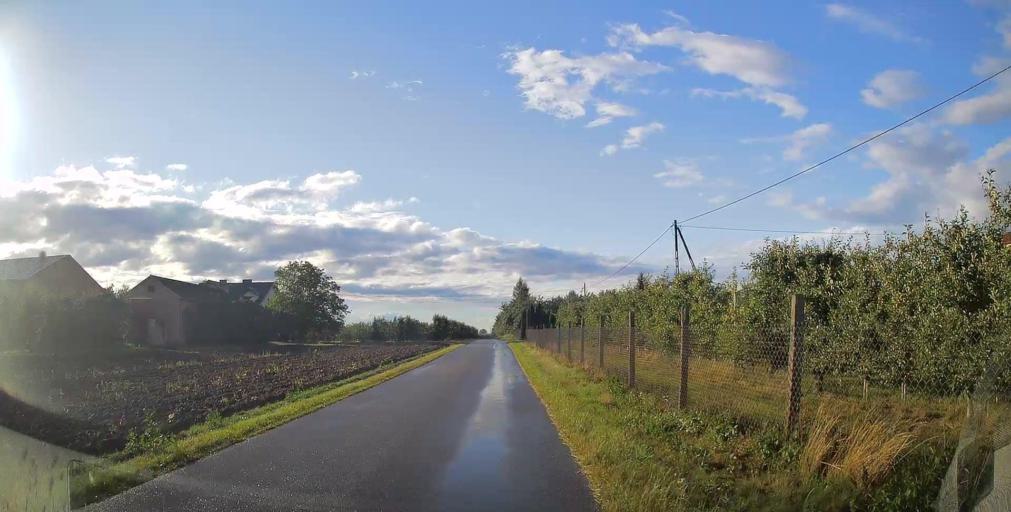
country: PL
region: Masovian Voivodeship
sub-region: Powiat grojecki
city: Goszczyn
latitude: 51.7500
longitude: 20.8854
